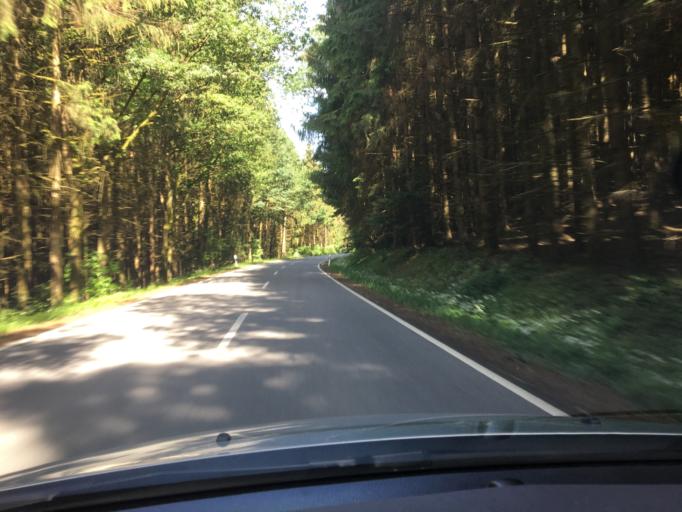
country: DE
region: Bavaria
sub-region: Upper Bavaria
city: Niedertaufkirchen
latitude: 48.3429
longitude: 12.5751
